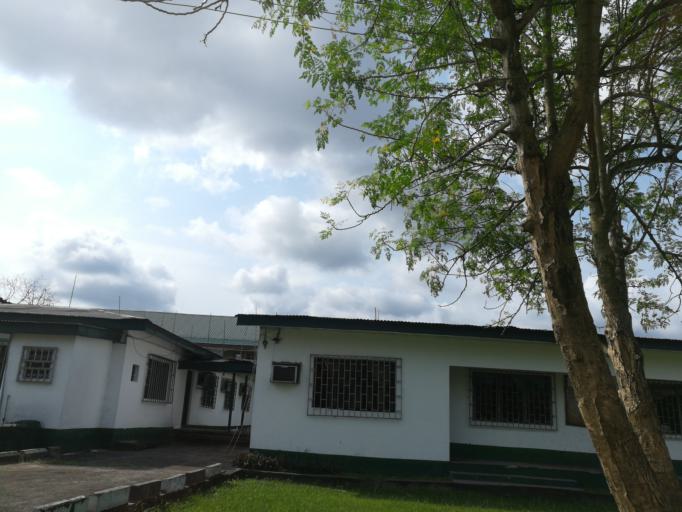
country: NG
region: Rivers
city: Okrika
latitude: 4.7523
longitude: 7.0988
